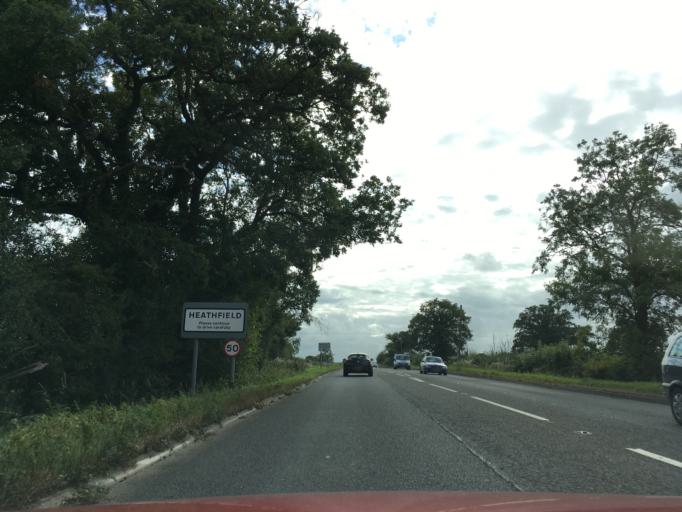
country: GB
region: England
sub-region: Gloucestershire
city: Berkeley
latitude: 51.6895
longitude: -2.4277
